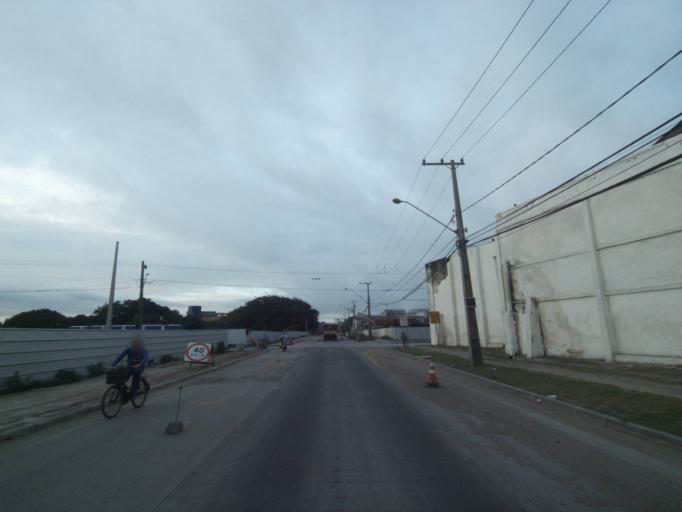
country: BR
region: Parana
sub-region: Paranagua
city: Paranagua
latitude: -25.5083
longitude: -48.5287
